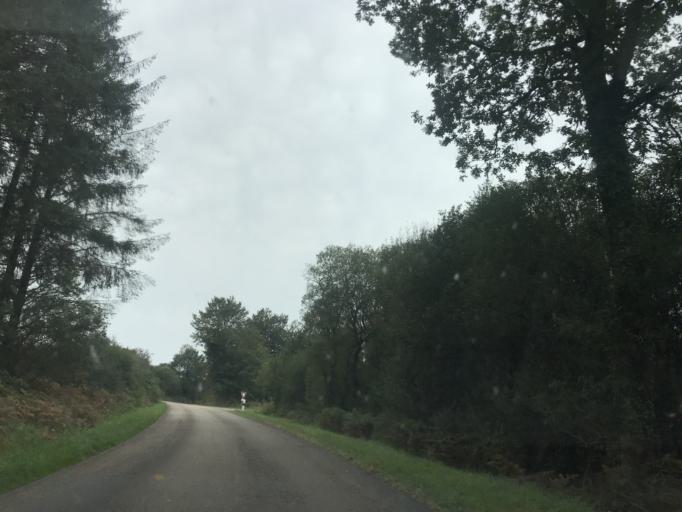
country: FR
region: Brittany
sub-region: Departement du Finistere
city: Plouneour-Menez
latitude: 48.3859
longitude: -3.8856
